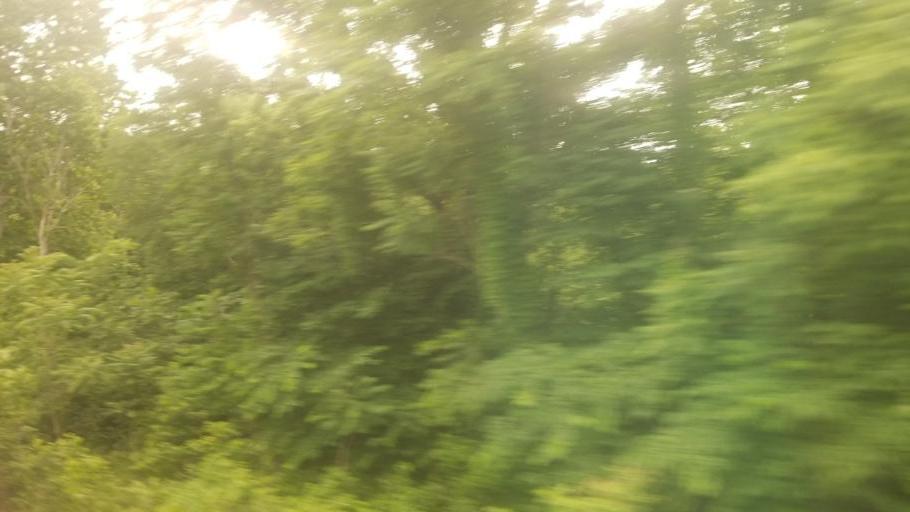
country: US
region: West Virginia
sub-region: Morgan County
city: Berkeley Springs
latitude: 39.5784
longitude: -78.4009
